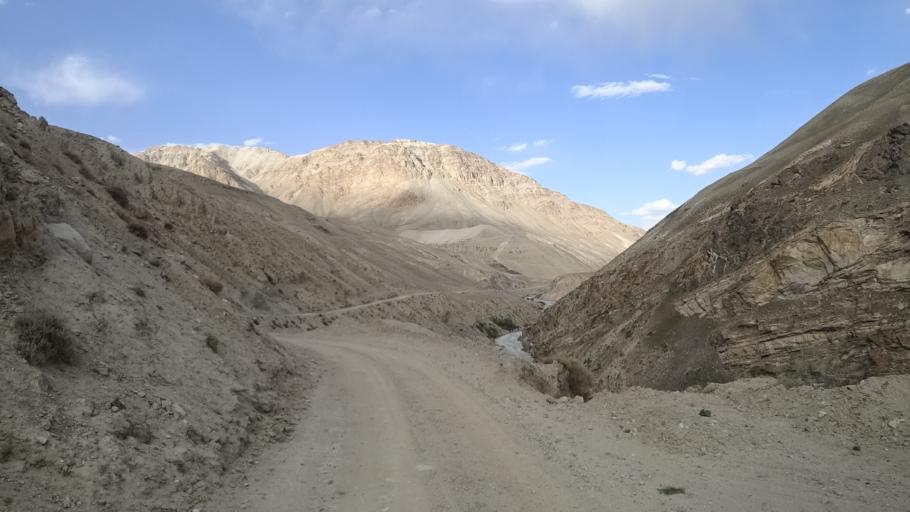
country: AF
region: Badakhshan
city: Khandud
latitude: 37.2313
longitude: 72.8128
